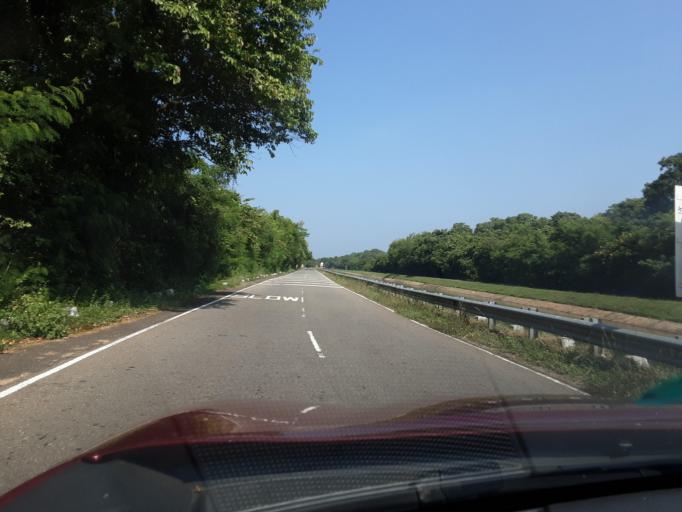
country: LK
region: Uva
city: Badulla
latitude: 7.2762
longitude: 81.0447
